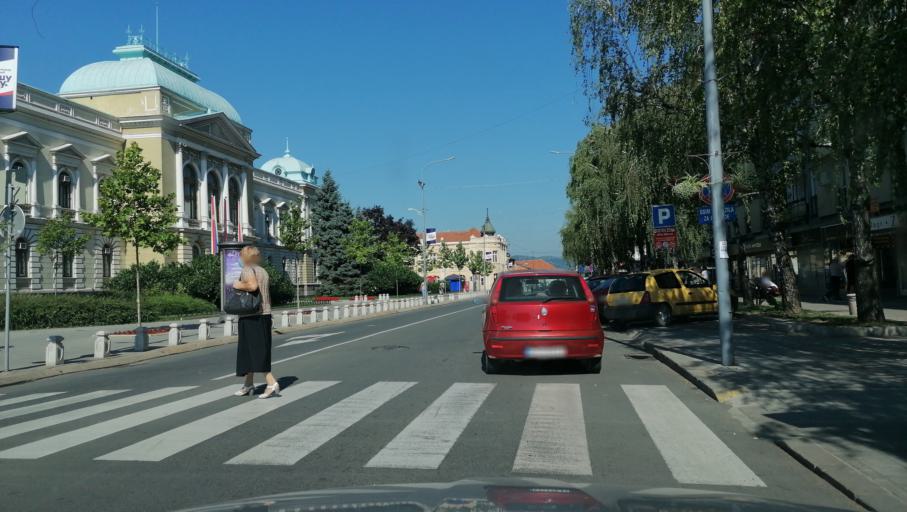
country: RS
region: Central Serbia
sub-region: Rasinski Okrug
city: Krusevac
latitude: 43.5832
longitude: 21.3257
